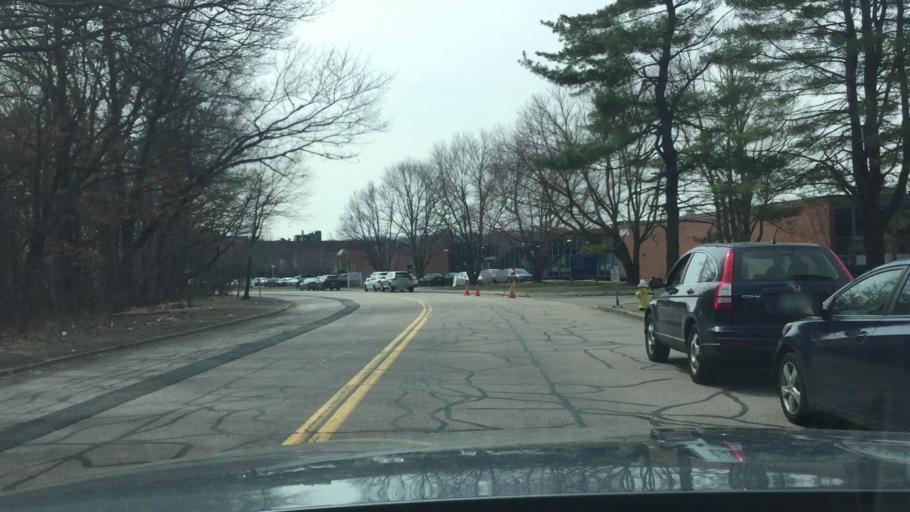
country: US
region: Massachusetts
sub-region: Norfolk County
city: Needham
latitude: 42.3009
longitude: -71.2127
